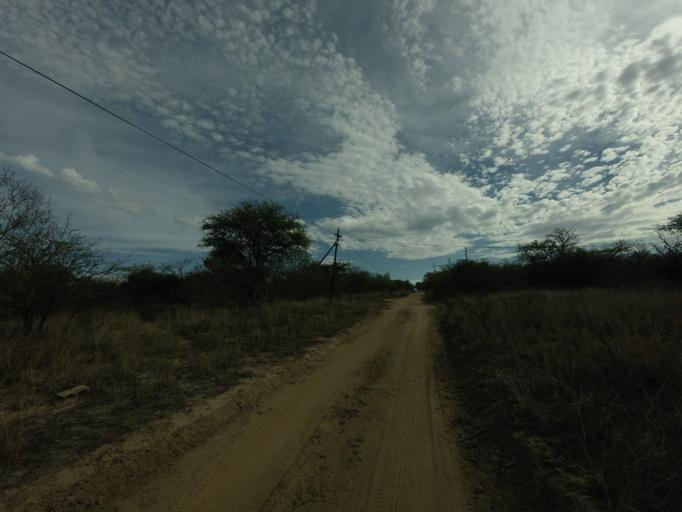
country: ZA
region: Limpopo
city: Thulamahashi
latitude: -24.5248
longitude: 31.1223
